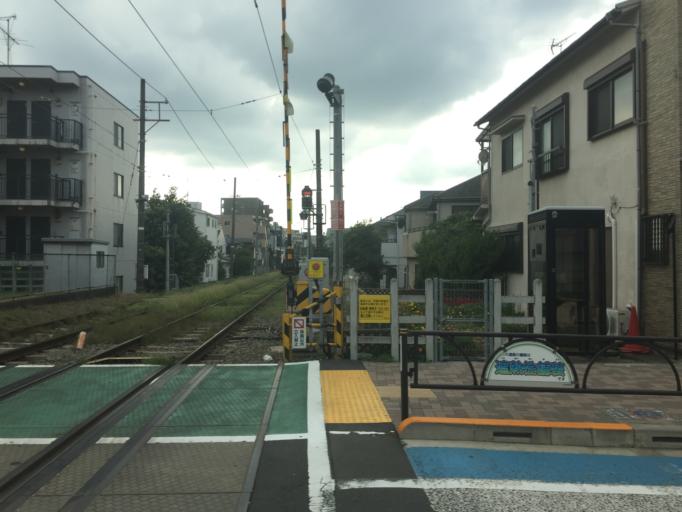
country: JP
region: Tokyo
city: Tokyo
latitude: 35.6436
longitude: 139.6503
